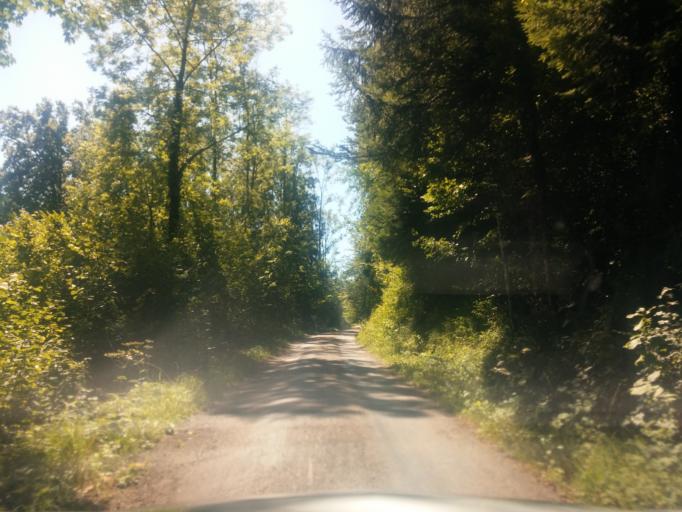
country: FR
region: Franche-Comte
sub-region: Departement du Jura
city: Saint-Lupicin
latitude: 46.4178
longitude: 5.7892
